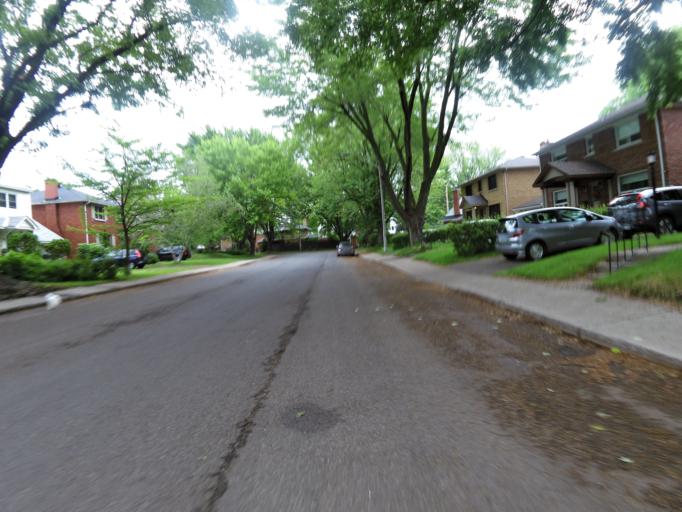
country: CA
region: Ontario
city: Ottawa
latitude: 45.3990
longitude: -75.6758
